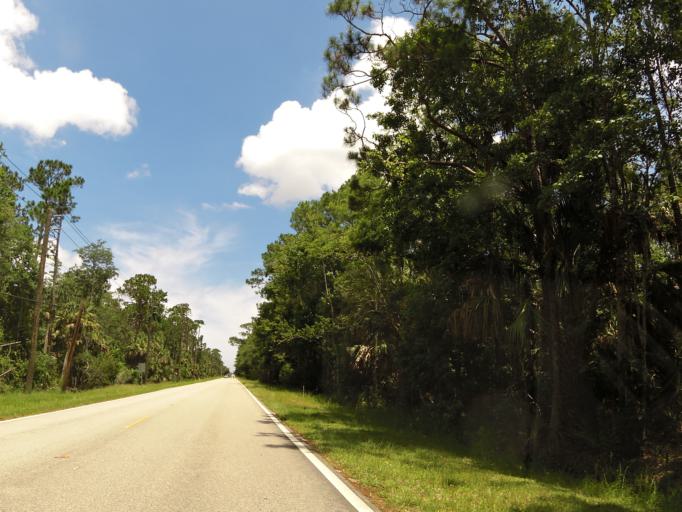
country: US
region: Florida
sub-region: Flagler County
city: Flagler Beach
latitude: 29.4035
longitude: -81.1764
